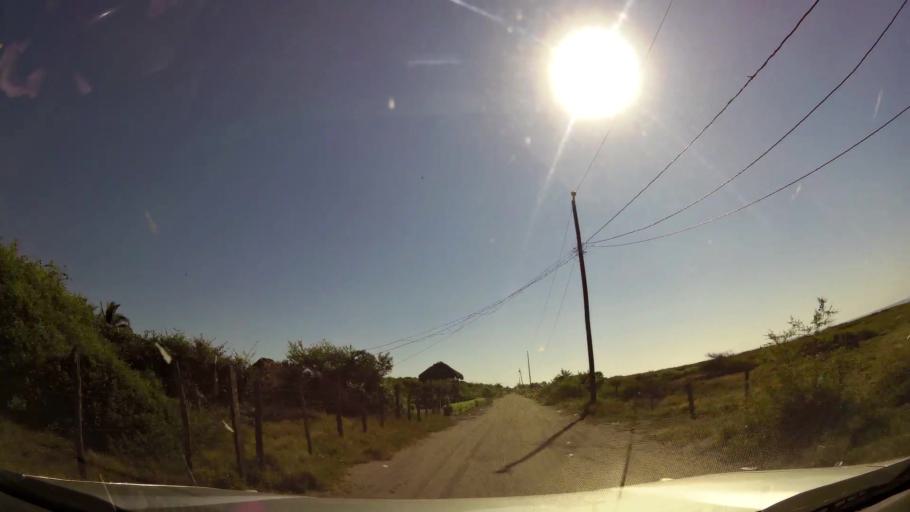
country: GT
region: Jutiapa
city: Pasaco
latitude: 13.8514
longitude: -90.3771
